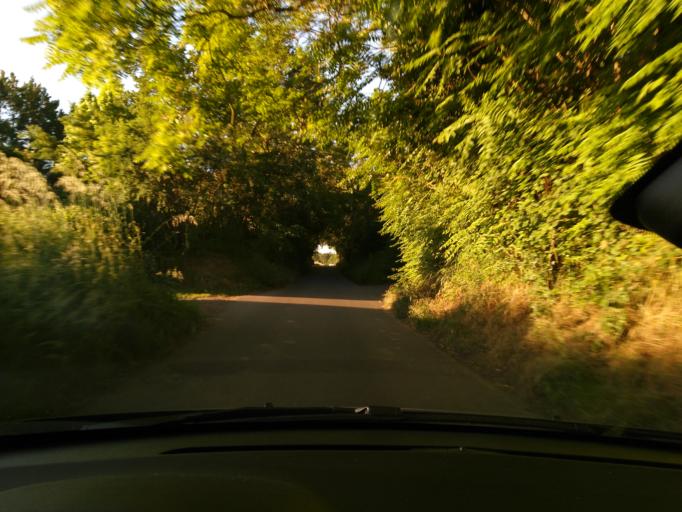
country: FR
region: Midi-Pyrenees
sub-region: Departement de la Haute-Garonne
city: Grenade
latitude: 43.7577
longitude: 1.2984
